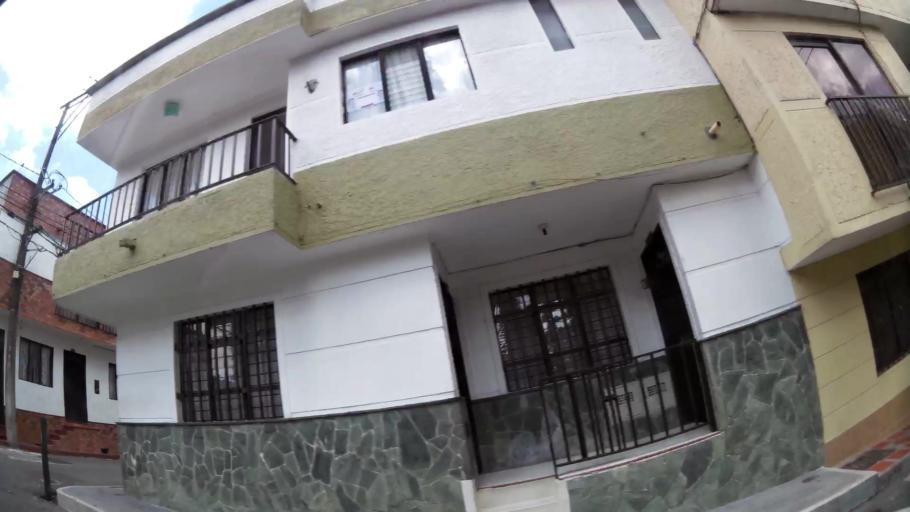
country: CO
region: Antioquia
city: La Estrella
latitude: 6.1592
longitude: -75.6467
